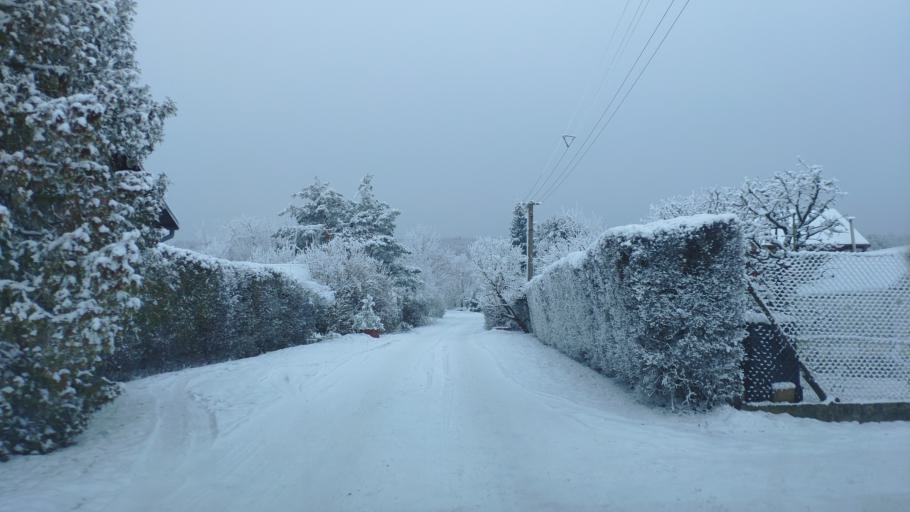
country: SK
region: Kosicky
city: Kosice
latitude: 48.6431
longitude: 21.1952
